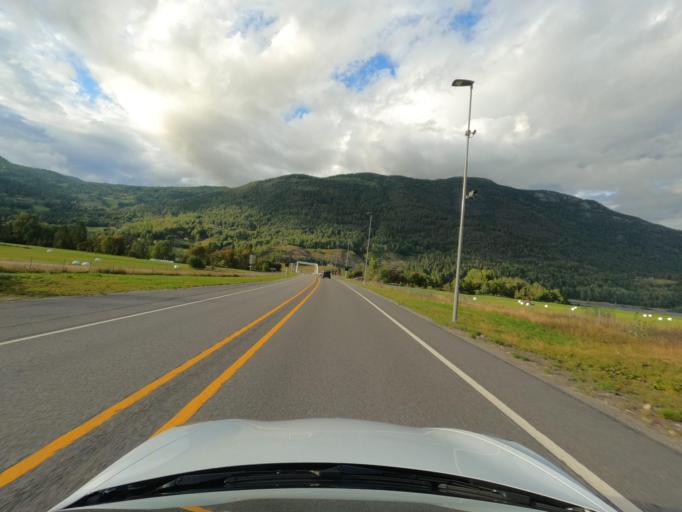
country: NO
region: Telemark
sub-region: Seljord
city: Seljord
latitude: 59.5983
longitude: 8.7154
